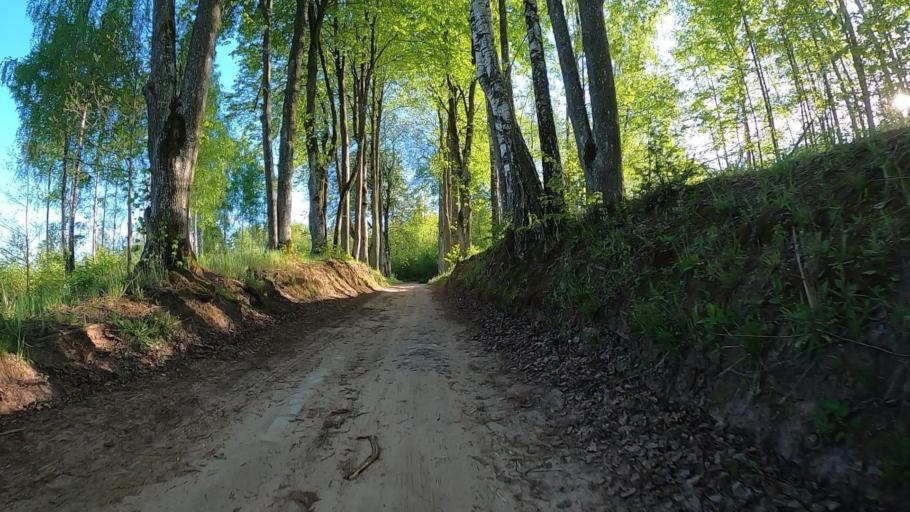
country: LV
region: Kekava
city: Kekava
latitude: 56.7777
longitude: 24.2952
